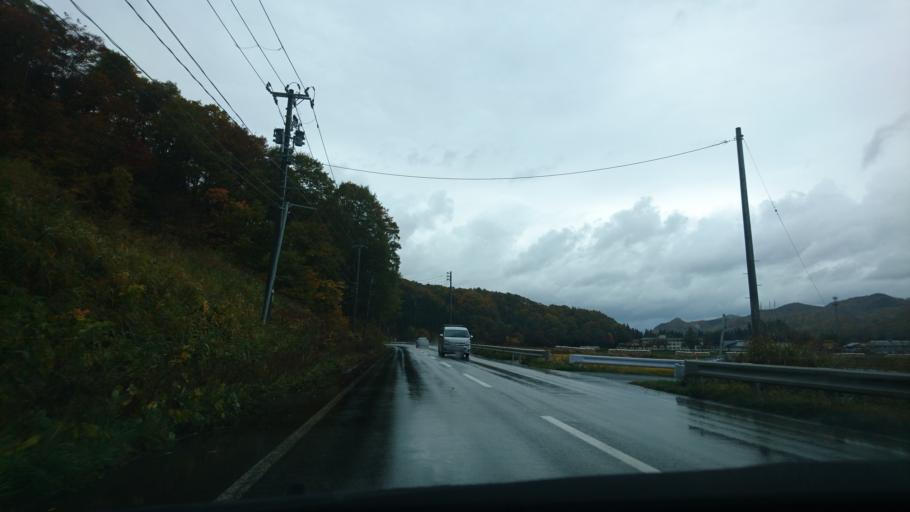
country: JP
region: Akita
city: Yokotemachi
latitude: 39.3488
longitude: 140.7657
